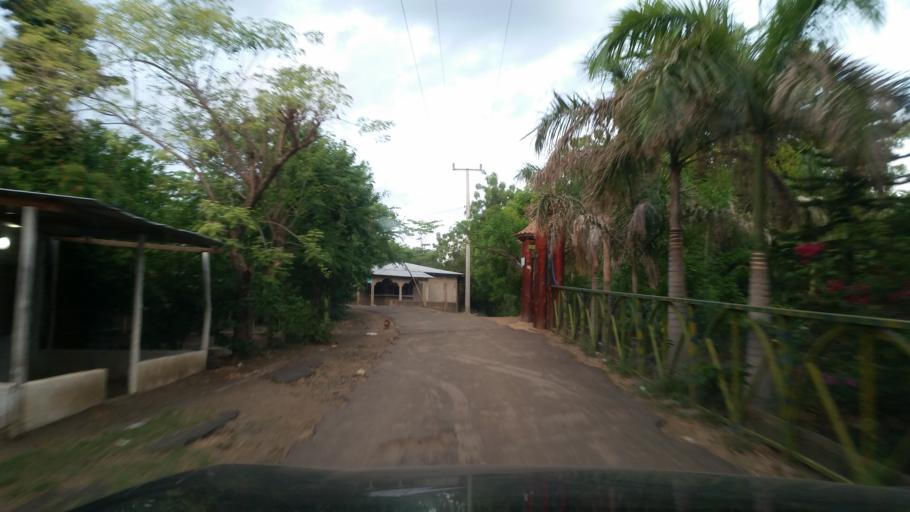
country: NI
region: Managua
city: Masachapa
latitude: 11.7716
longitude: -86.5028
